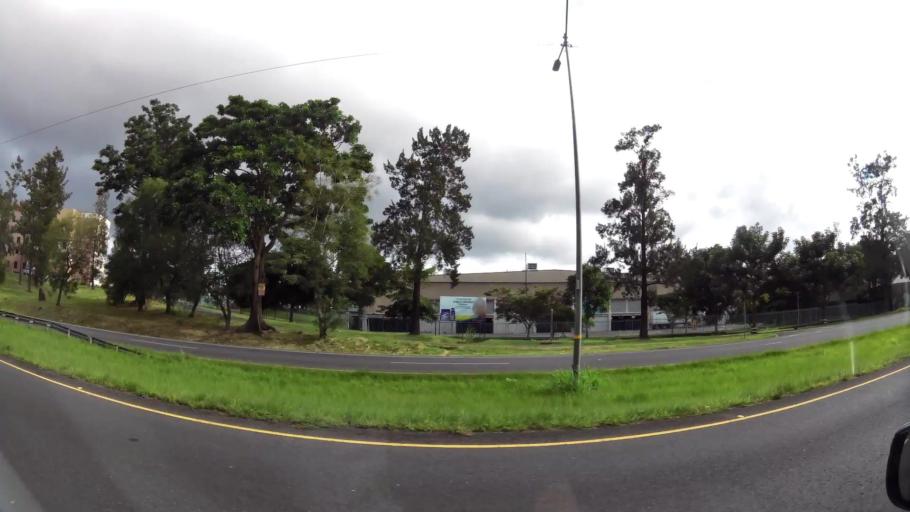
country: CR
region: Cartago
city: San Diego
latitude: 9.9090
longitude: -84.0167
